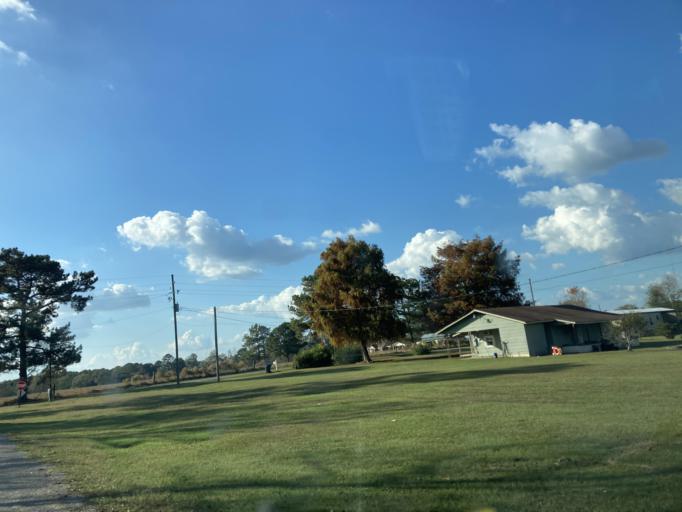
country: US
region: Mississippi
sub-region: Lamar County
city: Sumrall
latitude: 31.4320
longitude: -89.6371
